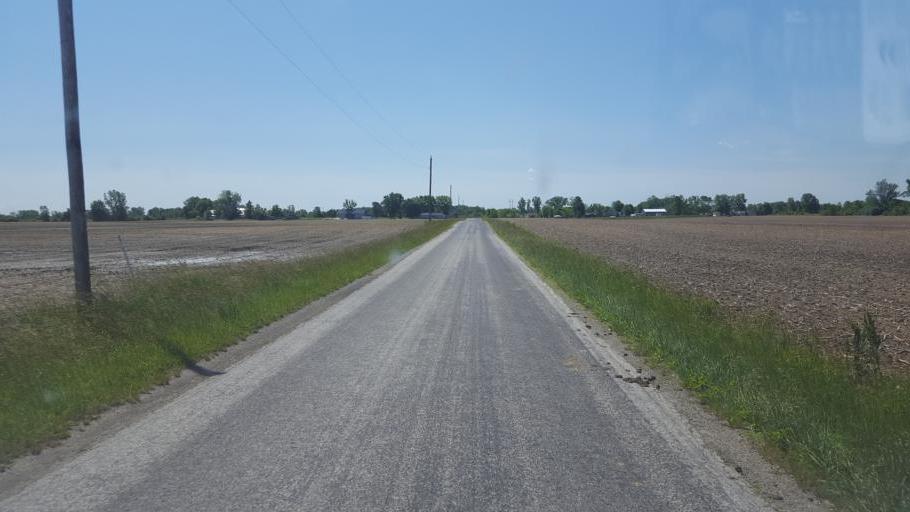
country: US
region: Ohio
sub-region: Union County
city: Richwood
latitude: 40.5763
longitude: -83.4072
